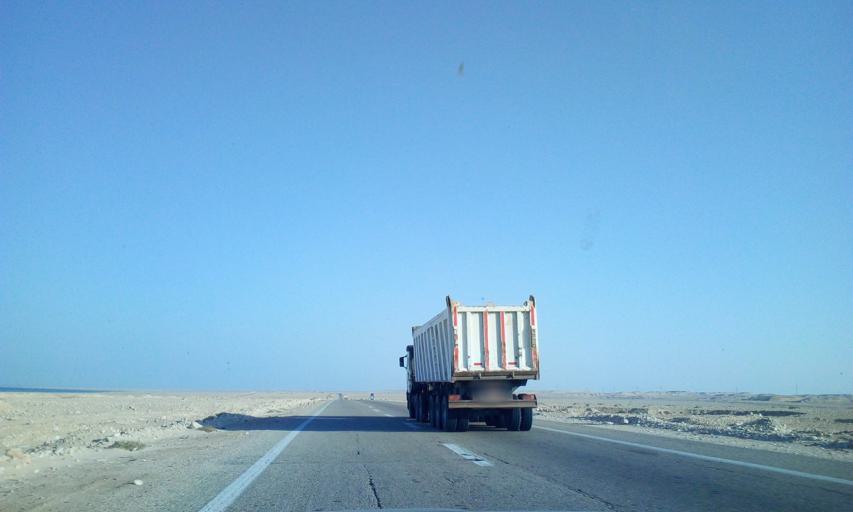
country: EG
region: As Suways
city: Ain Sukhna
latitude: 28.8301
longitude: 32.7142
